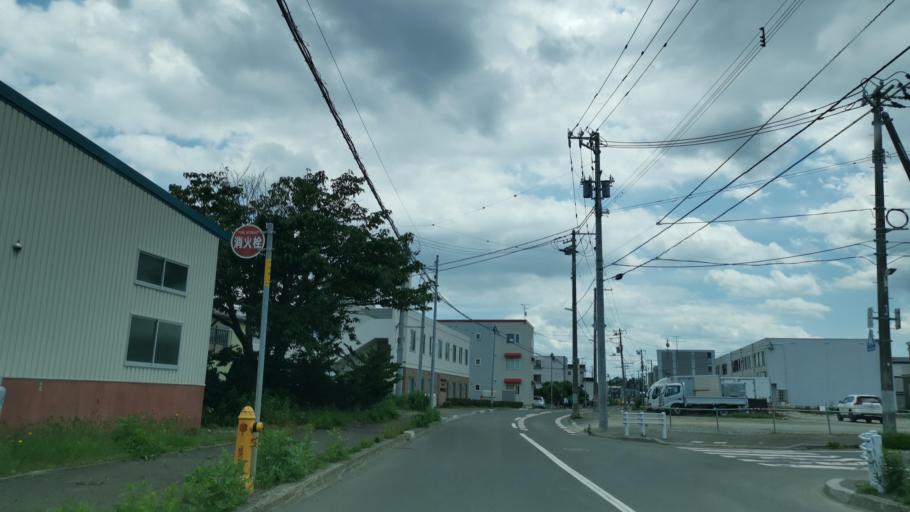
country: JP
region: Hokkaido
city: Sapporo
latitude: 43.0738
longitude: 141.4160
